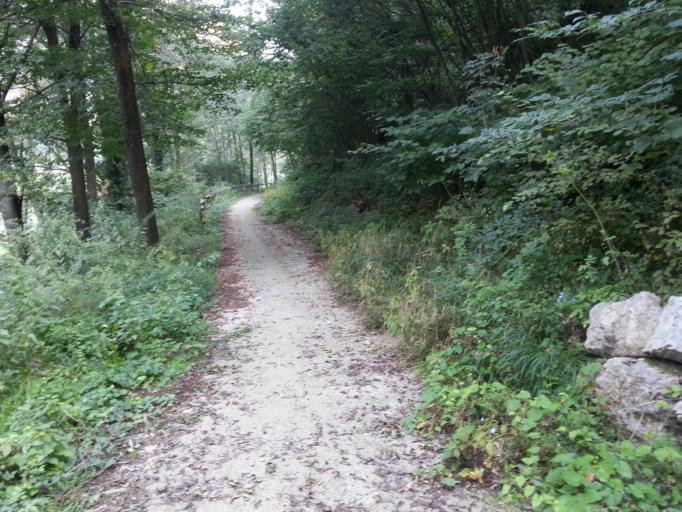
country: IT
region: Lombardy
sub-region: Provincia di Lecco
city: Ballabio
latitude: 45.9096
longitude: 9.4329
